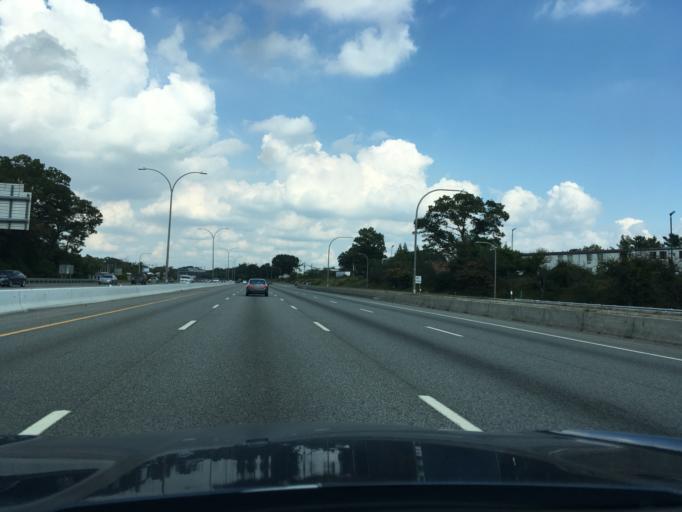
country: US
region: Rhode Island
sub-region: Providence County
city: Cranston
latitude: 41.7546
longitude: -71.4369
